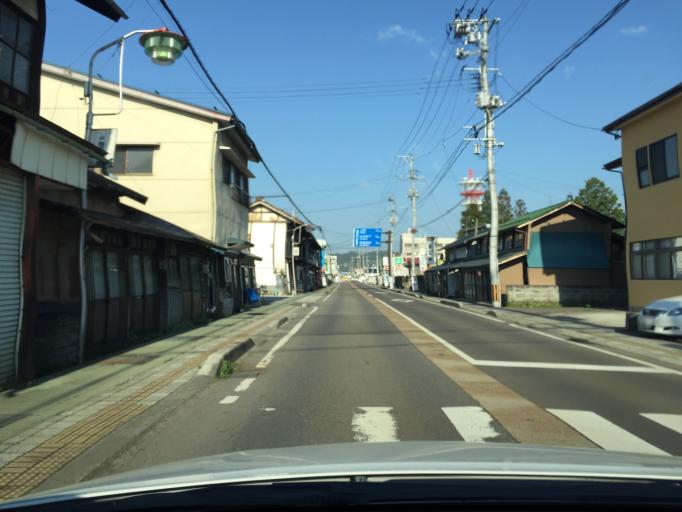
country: JP
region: Fukushima
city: Kitakata
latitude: 37.6550
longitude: 139.8792
